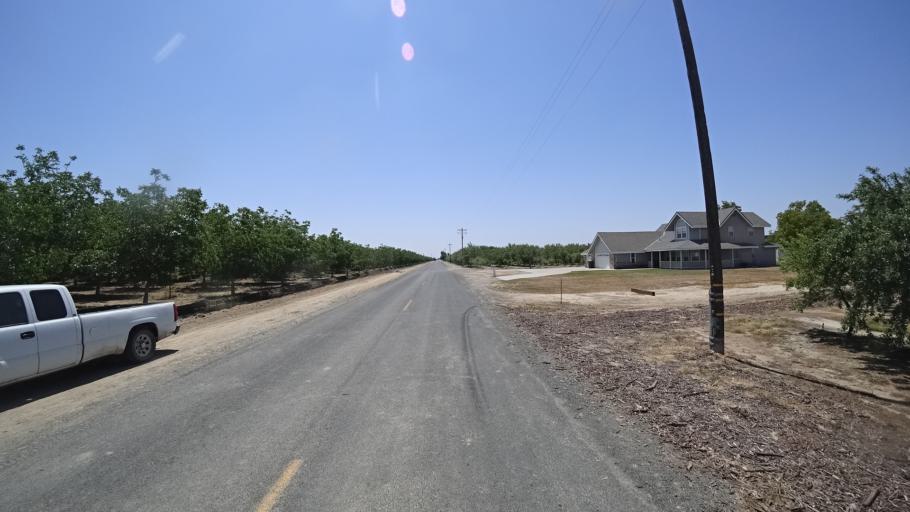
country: US
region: California
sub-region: Kings County
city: Armona
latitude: 36.2798
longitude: -119.7271
